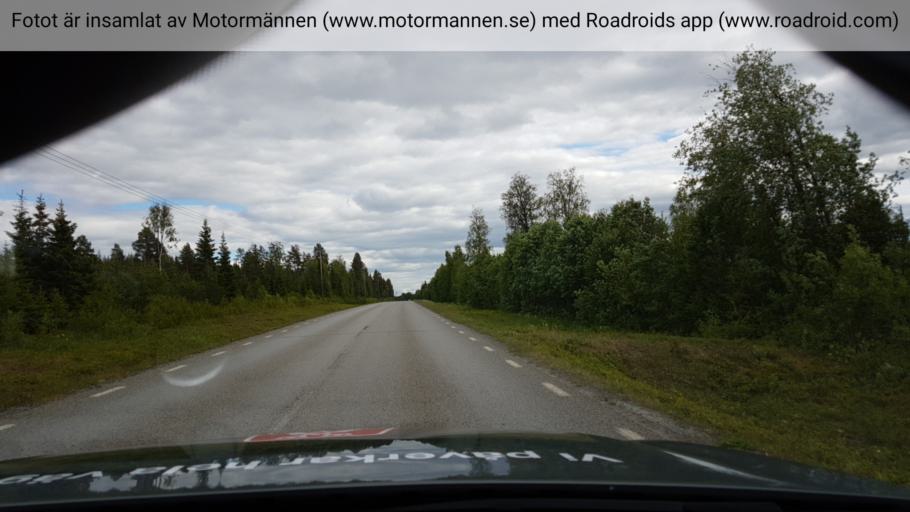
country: SE
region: Jaemtland
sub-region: Stroemsunds Kommun
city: Stroemsund
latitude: 63.9163
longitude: 15.5200
